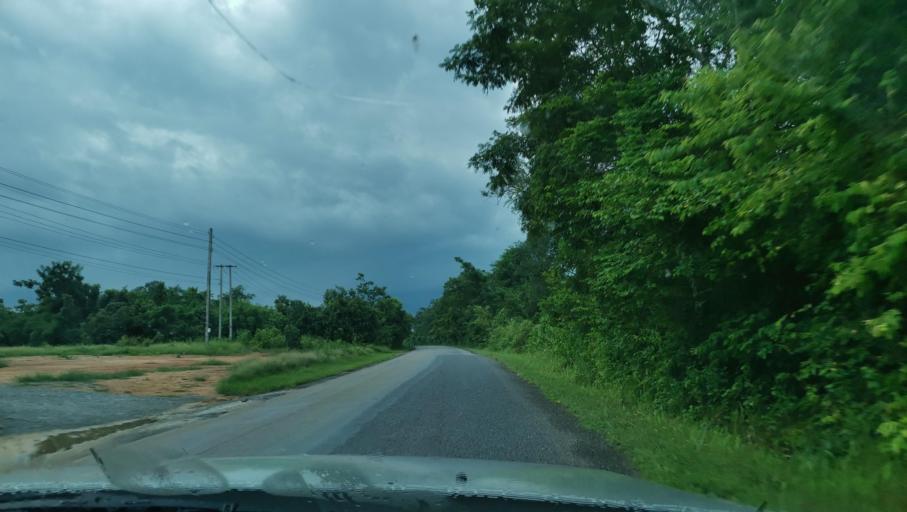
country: TH
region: Nakhon Phanom
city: Ban Phaeng
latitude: 17.8798
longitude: 104.4103
